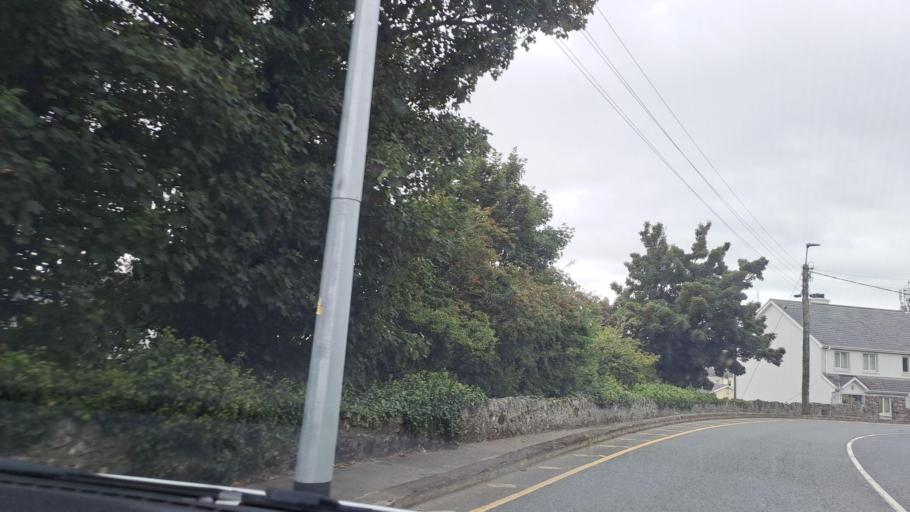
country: IE
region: Ulster
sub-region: County Monaghan
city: Carrickmacross
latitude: 53.9782
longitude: -6.7175
